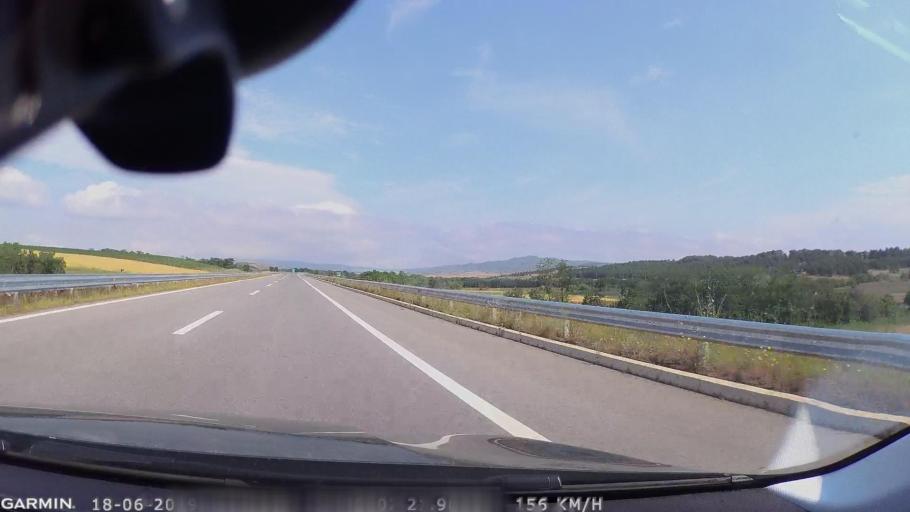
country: MK
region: Sveti Nikole
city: Gorobinci
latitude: 41.9062
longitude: 21.9077
